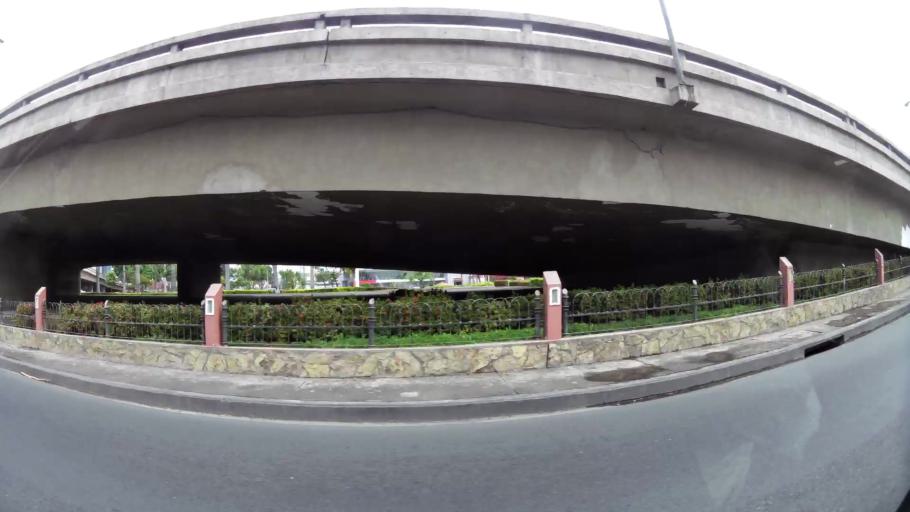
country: EC
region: Guayas
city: Eloy Alfaro
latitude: -2.1538
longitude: -79.8951
